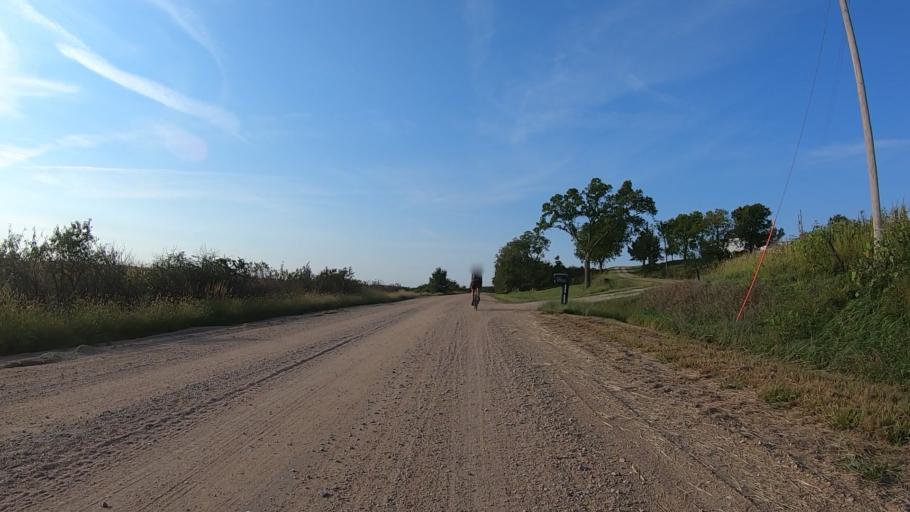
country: US
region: Kansas
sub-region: Marshall County
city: Blue Rapids
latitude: 39.6879
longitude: -96.7791
